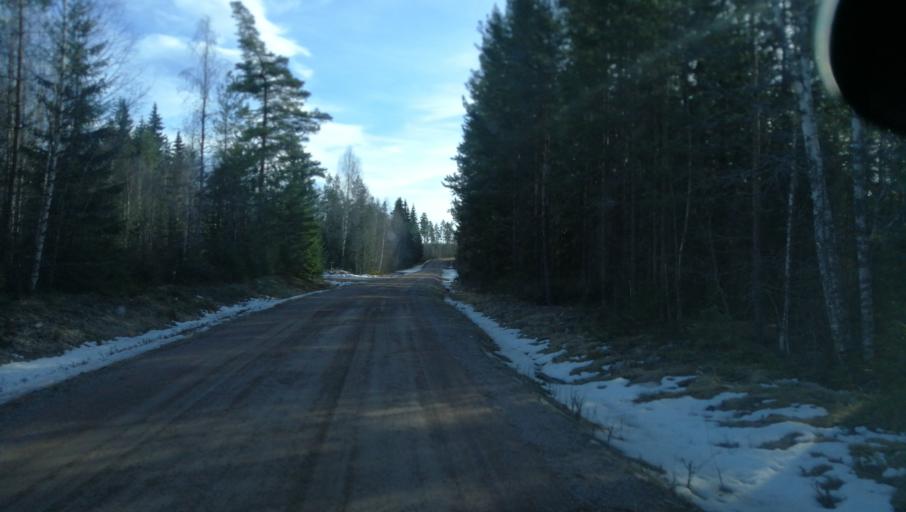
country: SE
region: Dalarna
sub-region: Vansbro Kommun
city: Vansbro
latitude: 60.8231
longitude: 14.1943
